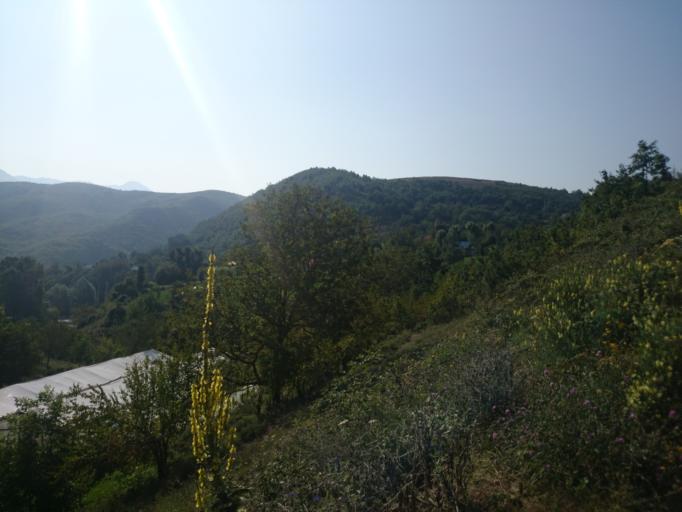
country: AL
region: Diber
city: Peshkopi
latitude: 41.6410
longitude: 20.4014
